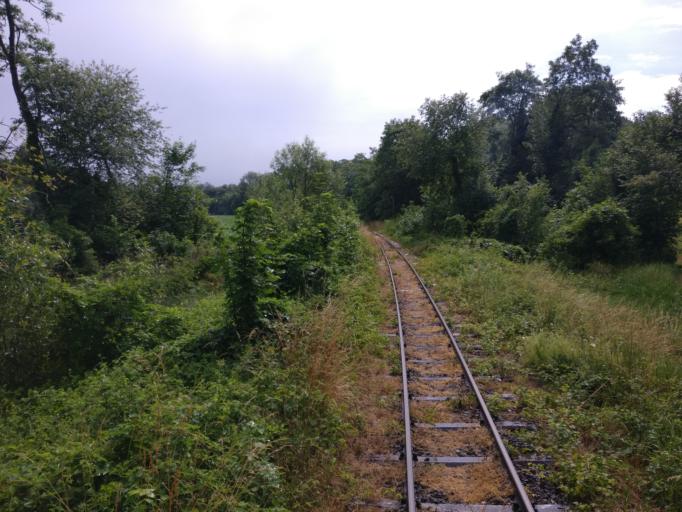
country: AT
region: Upper Austria
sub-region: Politischer Bezirk Steyr-Land
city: Garsten
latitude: 48.0400
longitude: 14.3869
